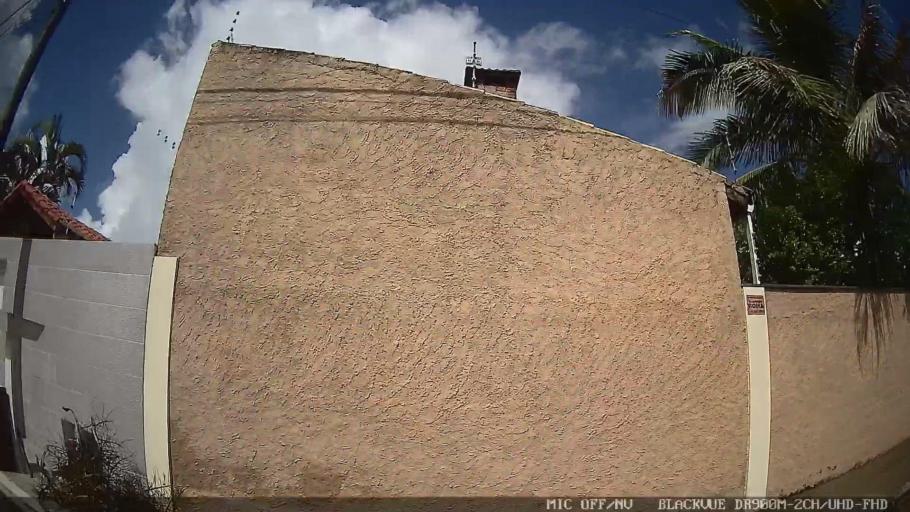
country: BR
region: Sao Paulo
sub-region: Itanhaem
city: Itanhaem
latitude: -24.1913
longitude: -46.8069
